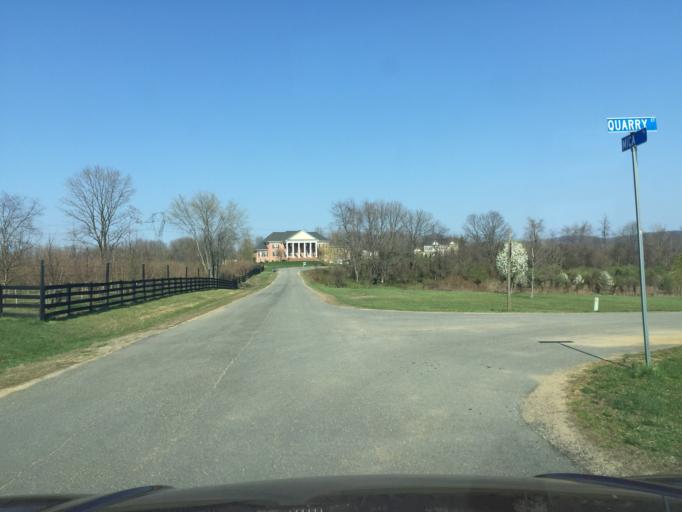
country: US
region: Maryland
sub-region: Frederick County
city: Brunswick
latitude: 39.2954
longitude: -77.5936
